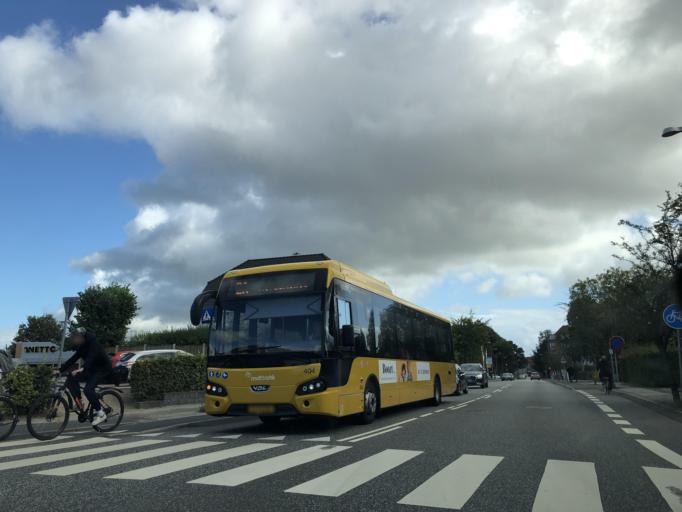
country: DK
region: Central Jutland
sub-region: Randers Kommune
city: Randers
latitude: 56.4676
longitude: 10.0206
